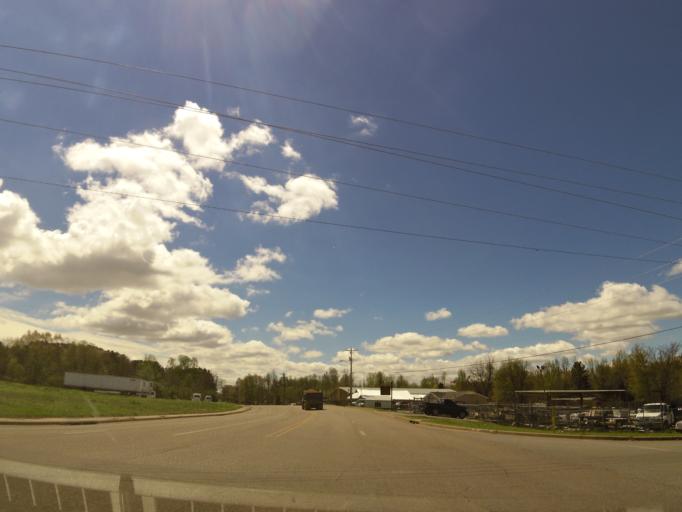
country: US
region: Arkansas
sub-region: Craighead County
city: Jonesboro
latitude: 35.8793
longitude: -90.7023
